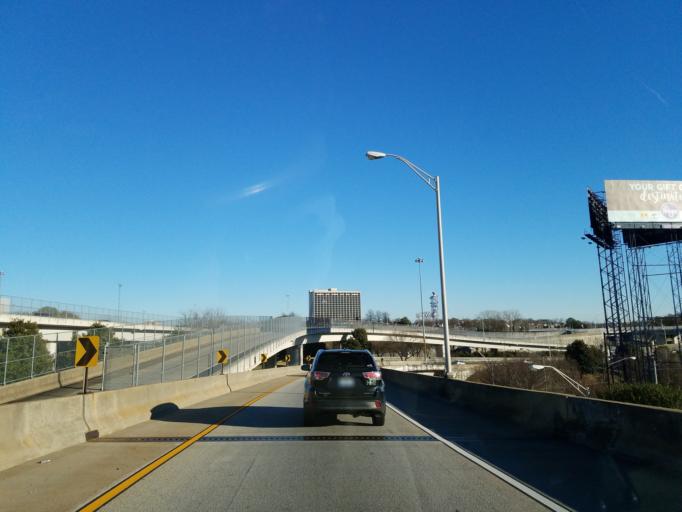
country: US
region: Georgia
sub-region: Fulton County
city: Atlanta
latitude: 33.7446
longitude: -84.3938
